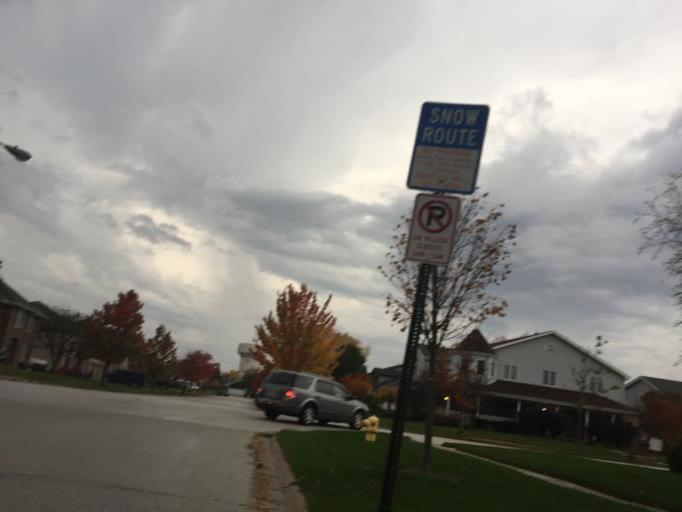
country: US
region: Illinois
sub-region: Cook County
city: Tinley Park
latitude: 41.5671
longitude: -87.8131
